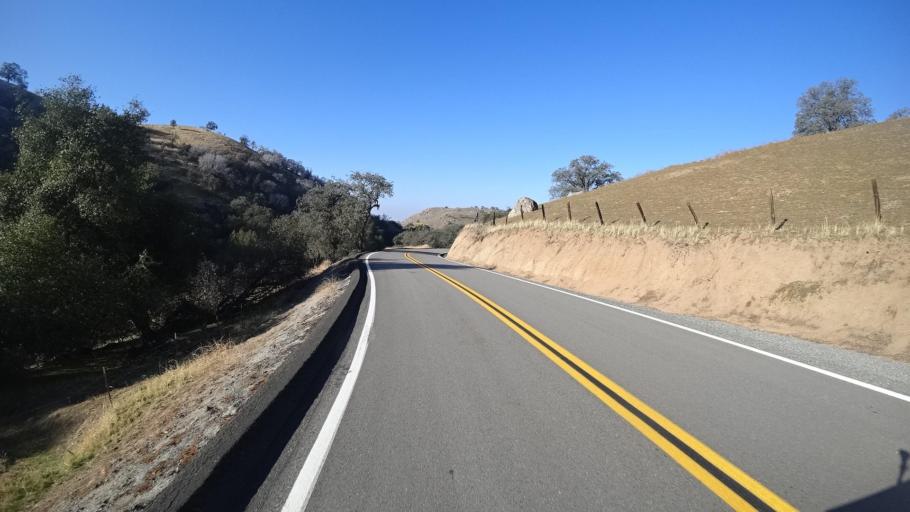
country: US
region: California
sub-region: Kern County
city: Alta Sierra
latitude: 35.7148
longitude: -118.8163
